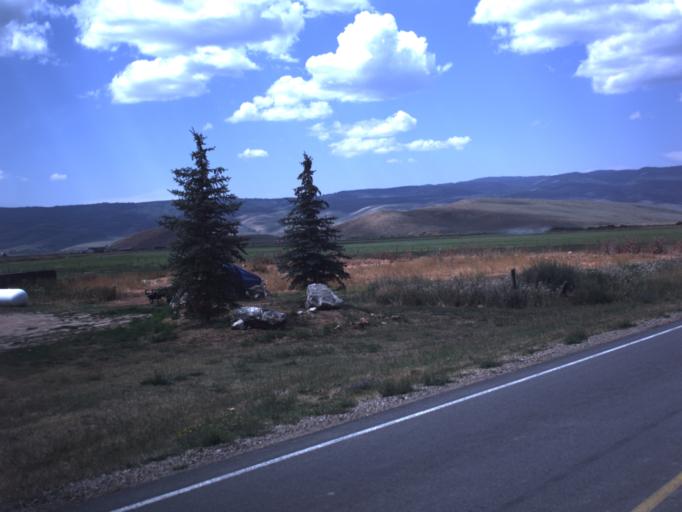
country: US
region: Utah
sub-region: Rich County
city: Randolph
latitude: 41.8322
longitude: -111.3240
